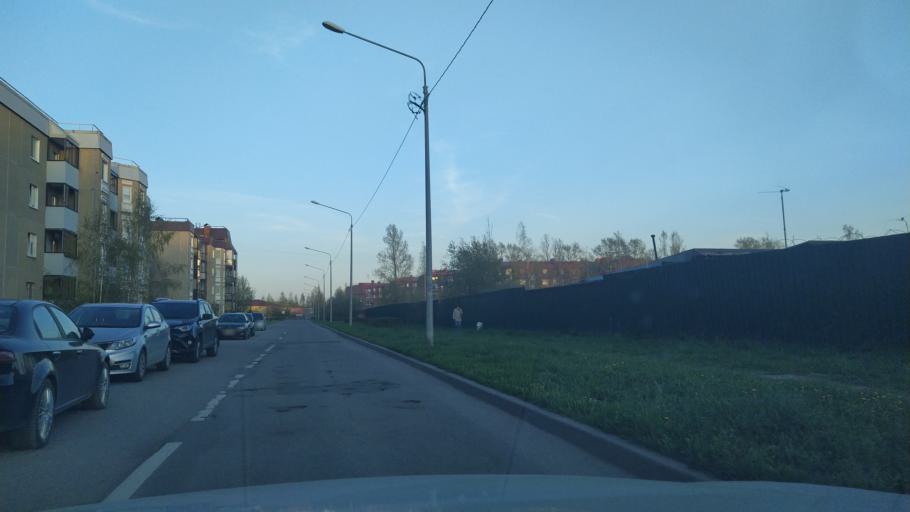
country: RU
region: St.-Petersburg
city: Pushkin
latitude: 59.7033
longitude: 30.3780
